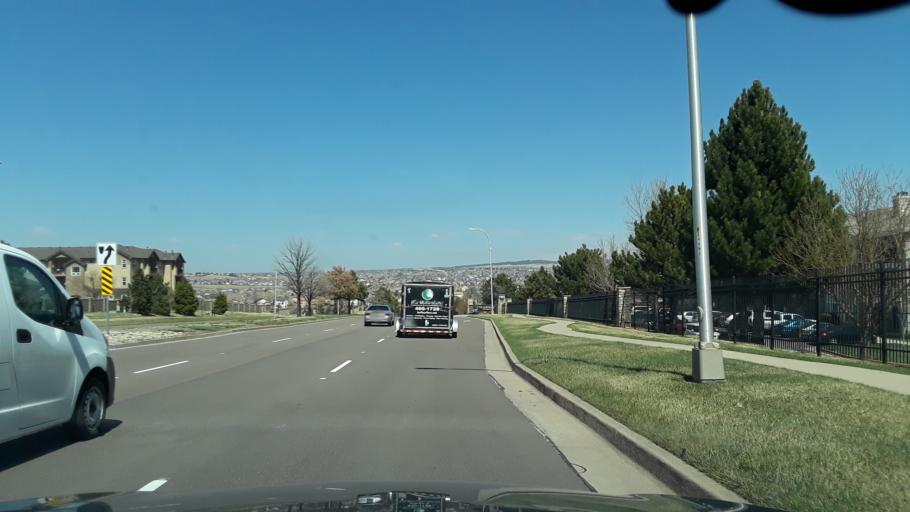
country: US
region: Colorado
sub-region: El Paso County
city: Cimarron Hills
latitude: 38.9217
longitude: -104.7384
